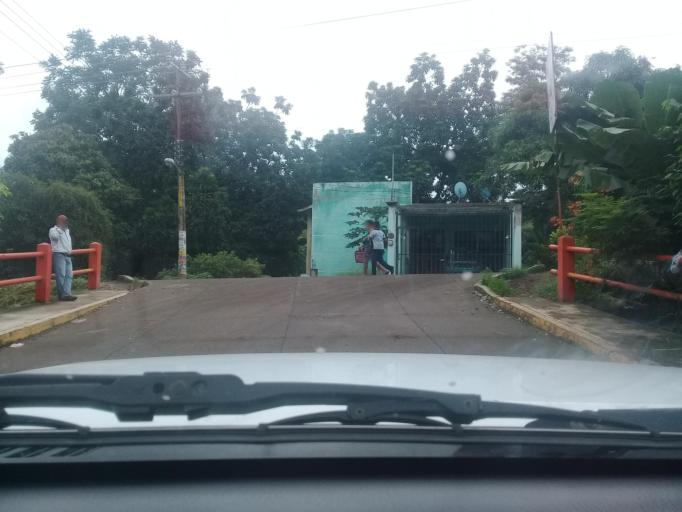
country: MX
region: Veracruz
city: Comoapan
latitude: 18.4060
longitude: -95.1764
